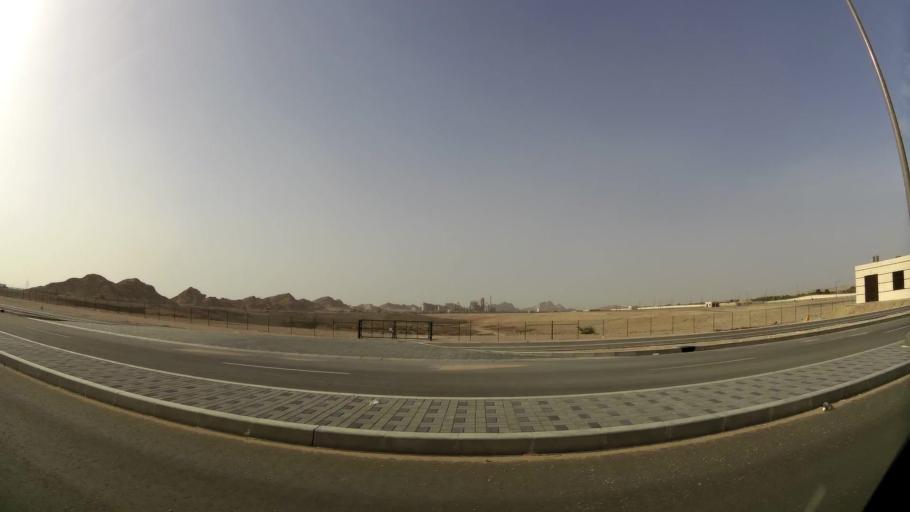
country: AE
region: Abu Dhabi
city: Al Ain
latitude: 24.1208
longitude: 55.7306
